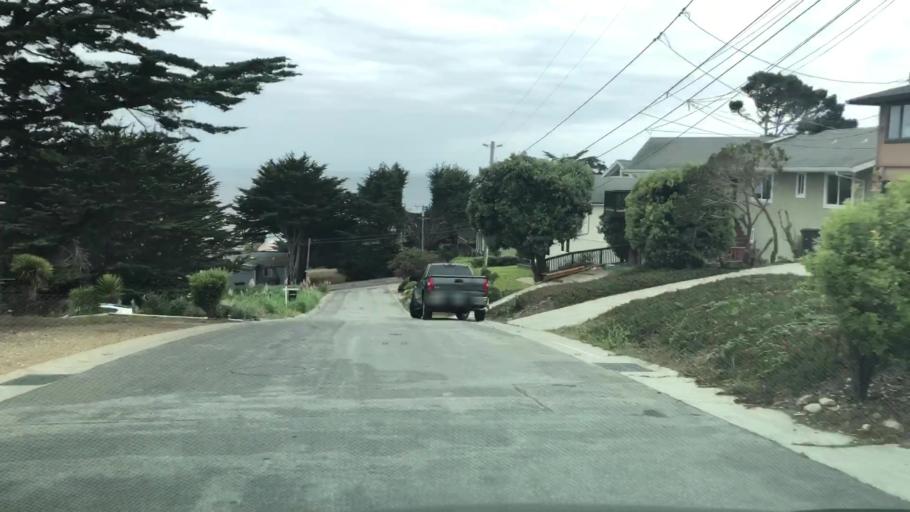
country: US
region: California
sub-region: San Mateo County
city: Montara
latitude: 37.5372
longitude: -122.5155
